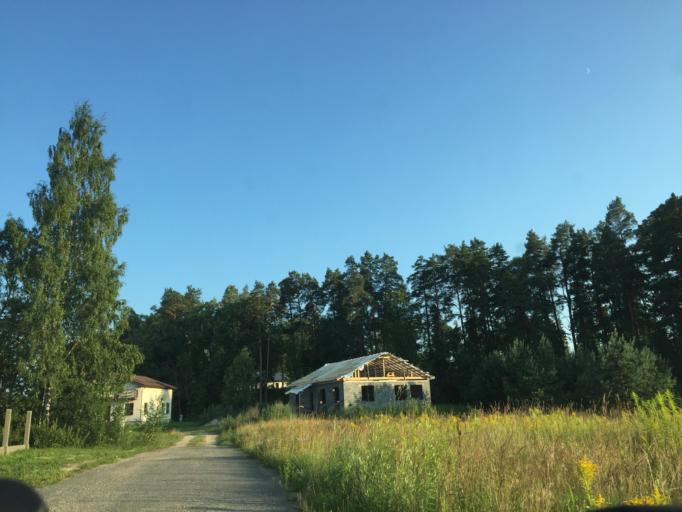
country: LV
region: Garkalne
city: Garkalne
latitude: 56.9801
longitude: 24.3795
